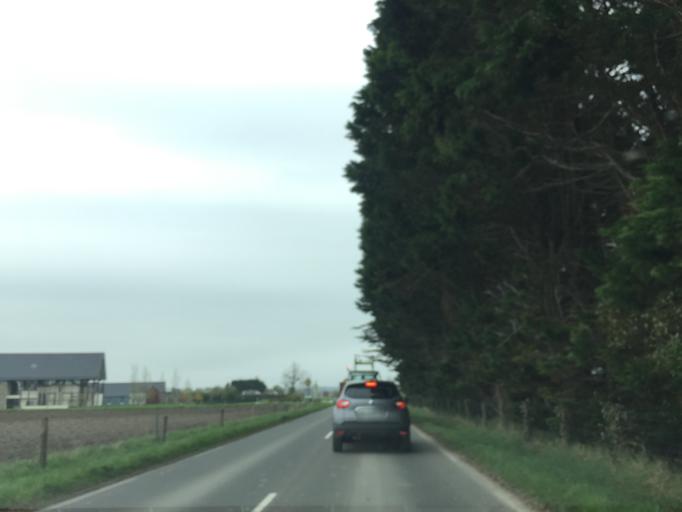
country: FR
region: Brittany
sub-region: Departement d'Ille-et-Vilaine
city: Cherrueix
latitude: 48.6023
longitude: -1.7125
